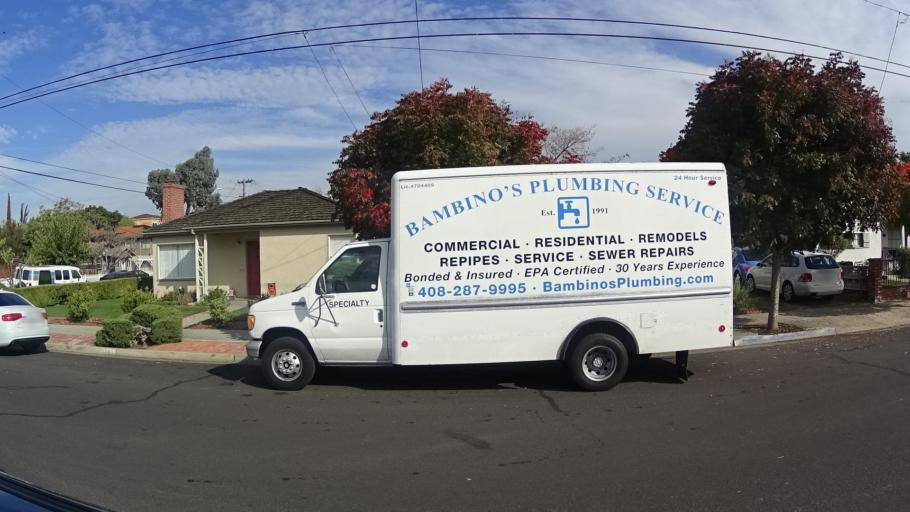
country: US
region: California
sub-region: Santa Clara County
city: Santa Clara
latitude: 37.3513
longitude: -121.9525
